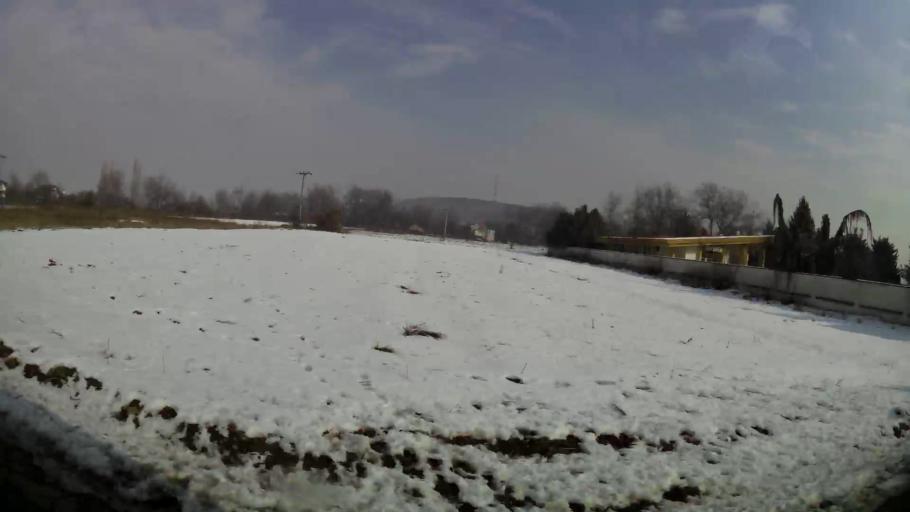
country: MK
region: Suto Orizari
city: Suto Orizare
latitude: 42.0147
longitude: 21.3885
